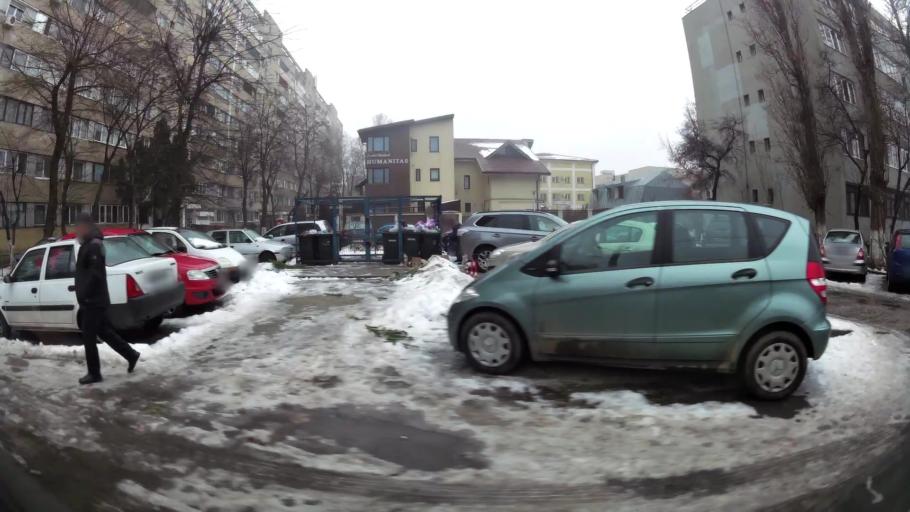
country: RO
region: Ilfov
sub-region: Comuna Chiajna
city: Rosu
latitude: 44.4369
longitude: 26.0161
